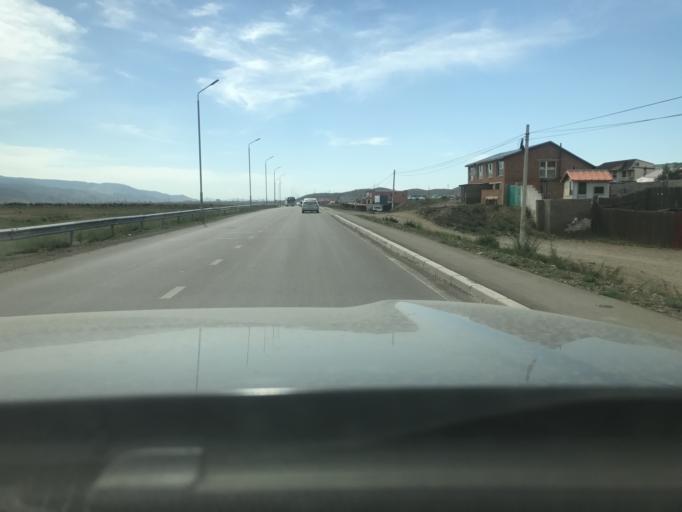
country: MN
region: Ulaanbaatar
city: Ulaanbaatar
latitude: 47.9160
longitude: 107.0889
